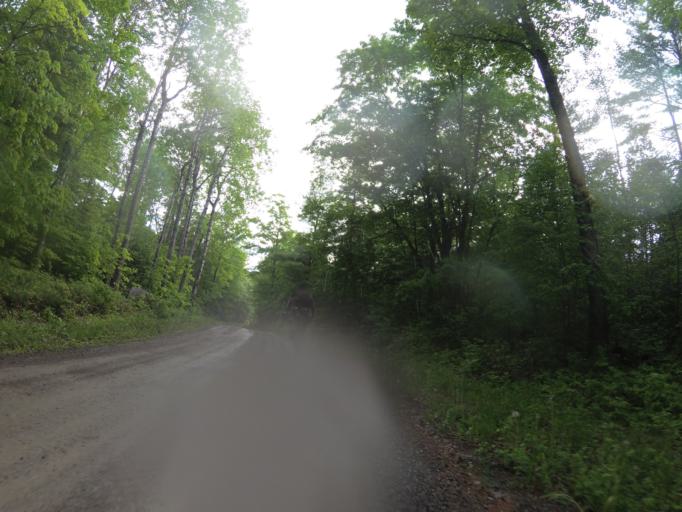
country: CA
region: Ontario
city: Renfrew
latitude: 45.1839
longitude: -76.9097
